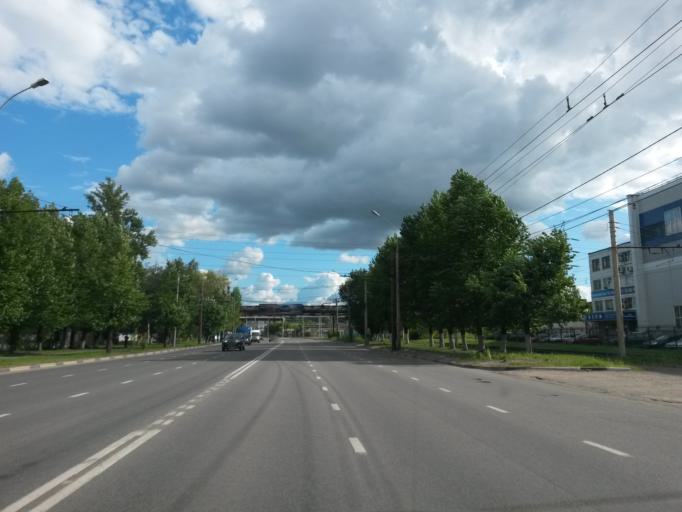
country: RU
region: Jaroslavl
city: Yaroslavl
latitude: 57.6544
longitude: 39.8452
